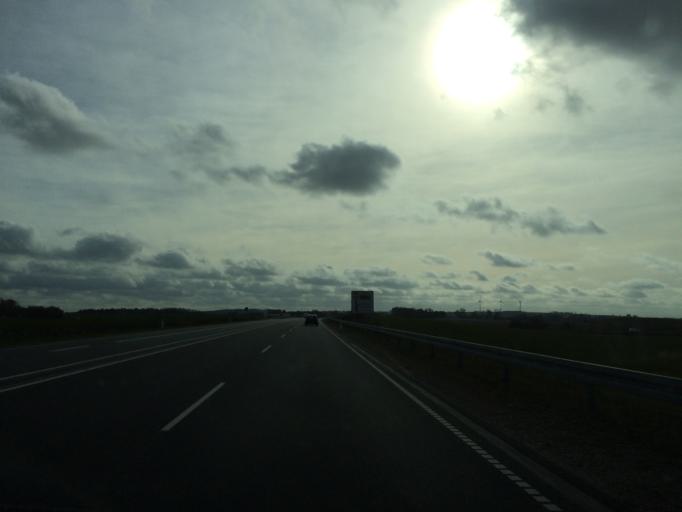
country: DK
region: Central Jutland
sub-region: Randers Kommune
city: Assentoft
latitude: 56.4232
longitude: 10.1076
